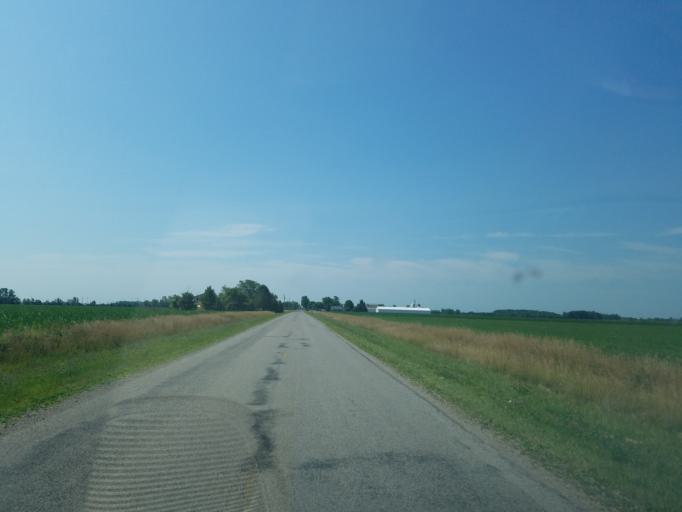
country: US
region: Ohio
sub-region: Van Wert County
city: Van Wert
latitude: 40.9221
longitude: -84.6296
